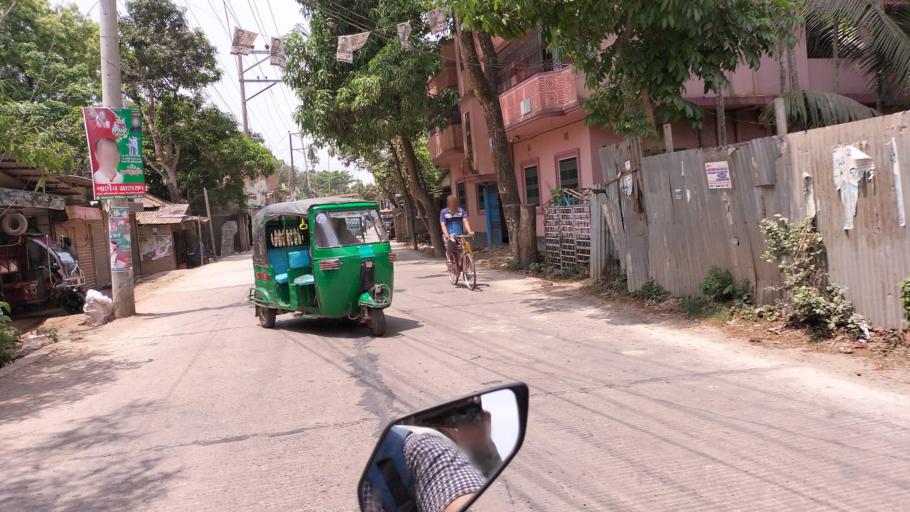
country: BD
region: Dhaka
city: Azimpur
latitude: 23.7334
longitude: 90.2699
